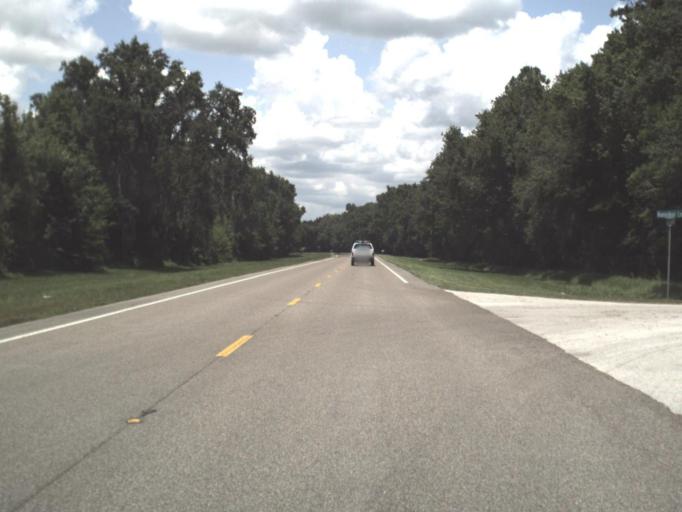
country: US
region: Florida
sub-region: Hernando County
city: North Brooksville
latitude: 28.6014
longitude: -82.4008
